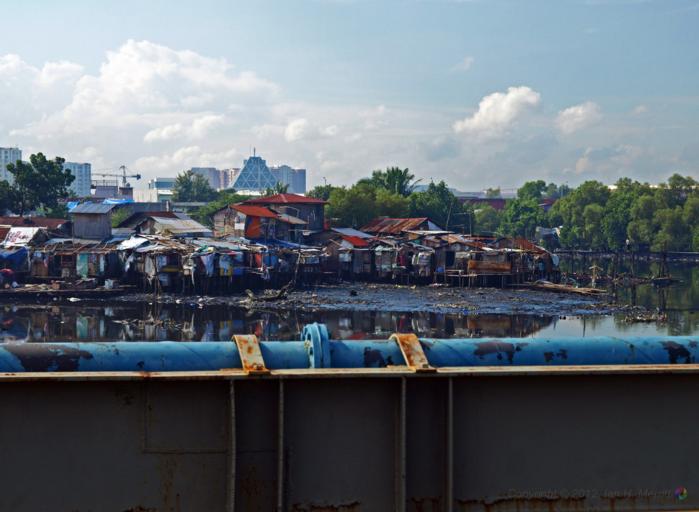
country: PH
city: Sambayanihan People's Village
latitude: 14.4987
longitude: 120.9938
